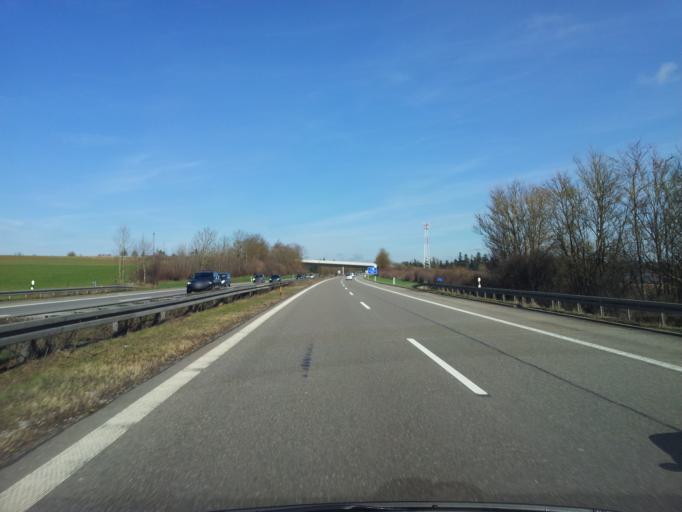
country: DE
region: Baden-Wuerttemberg
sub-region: Freiburg Region
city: Deisslingen
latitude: 48.1293
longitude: 8.5730
